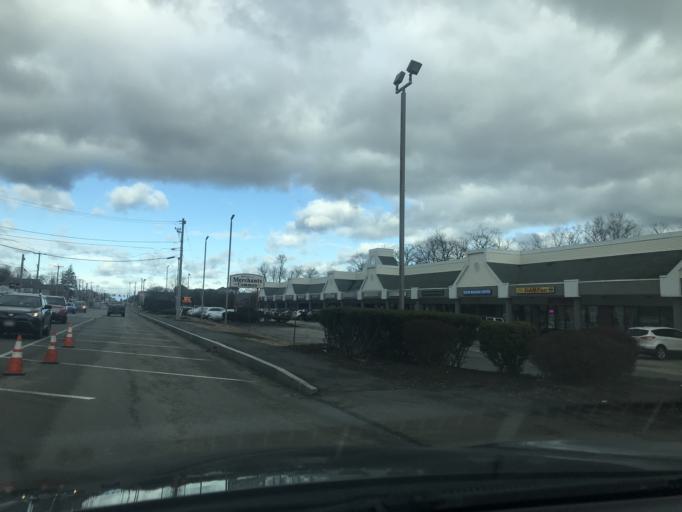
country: US
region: Massachusetts
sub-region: Plymouth County
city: Rockland
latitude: 42.1485
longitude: -70.9551
